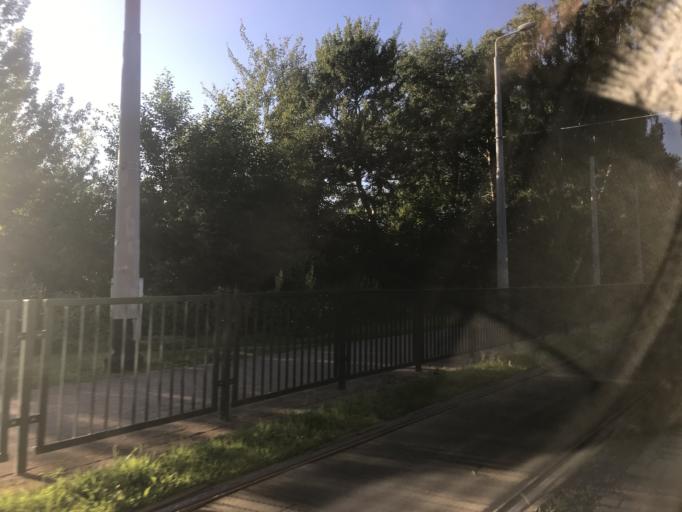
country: PL
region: Pomeranian Voivodeship
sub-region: Sopot
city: Sopot
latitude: 54.4227
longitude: 18.5911
